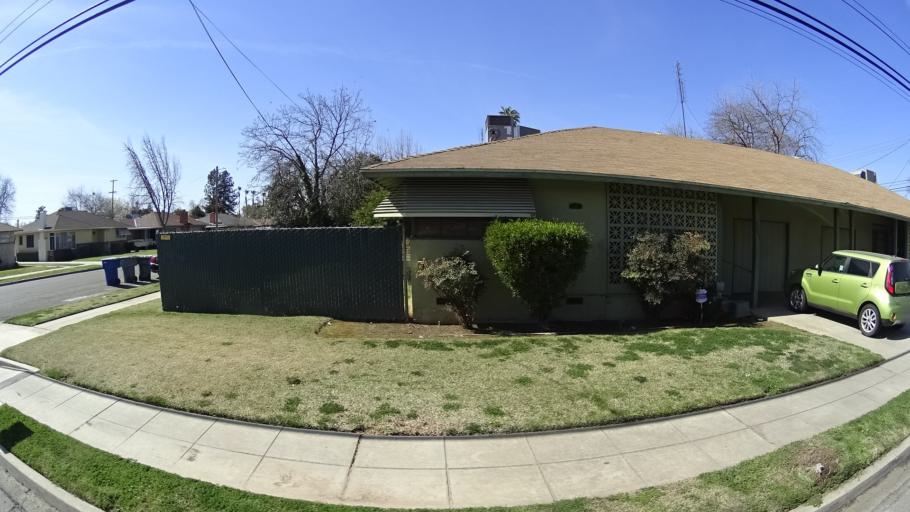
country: US
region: California
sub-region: Fresno County
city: Fresno
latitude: 36.7842
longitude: -119.8087
